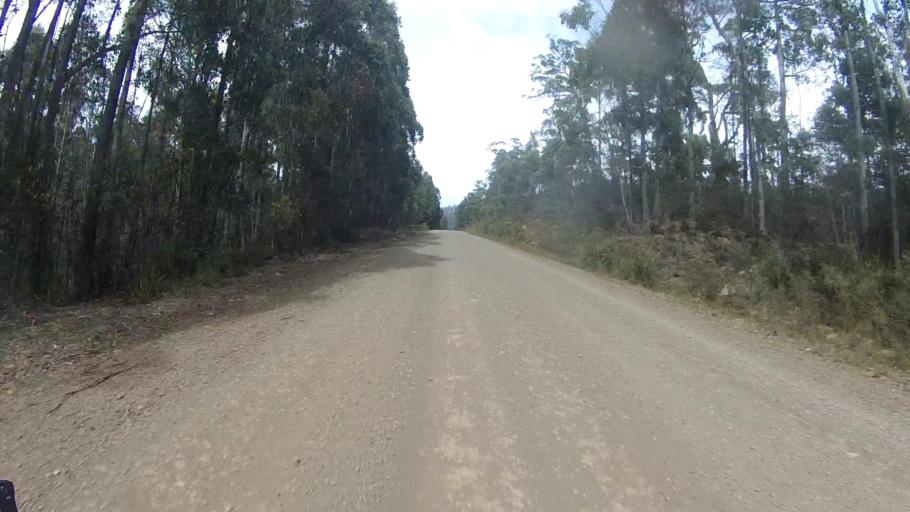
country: AU
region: Tasmania
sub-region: Sorell
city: Sorell
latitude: -42.6854
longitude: 147.8783
